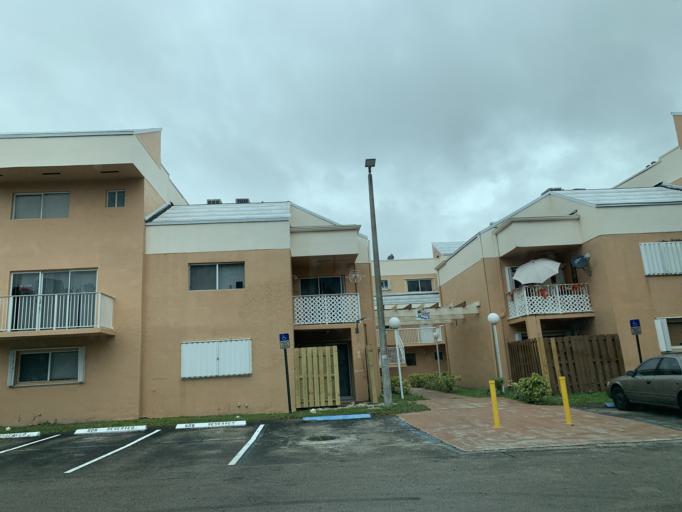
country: US
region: Florida
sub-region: Miami-Dade County
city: Kendall West
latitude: 25.6935
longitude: -80.4351
